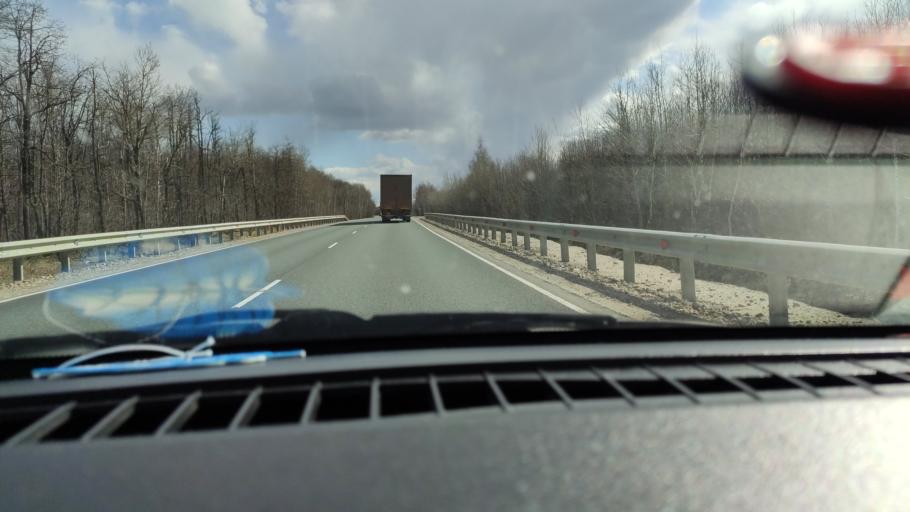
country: RU
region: Saratov
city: Khvalynsk
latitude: 52.4803
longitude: 48.0129
